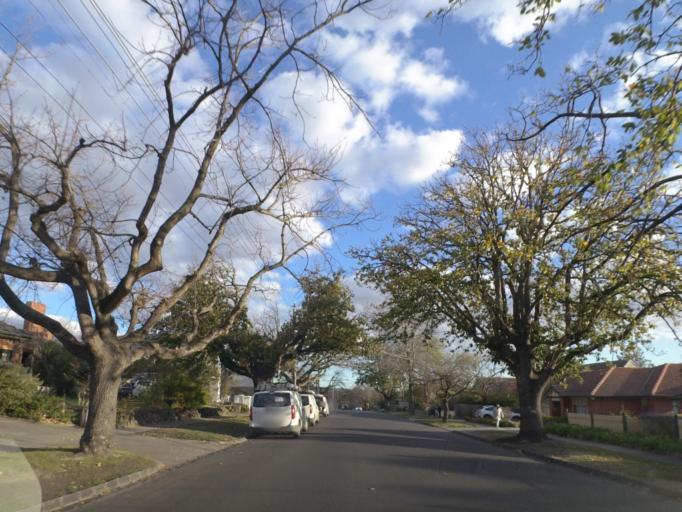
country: AU
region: Victoria
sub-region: Whitehorse
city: Surrey Hills
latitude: -37.8385
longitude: 145.0929
